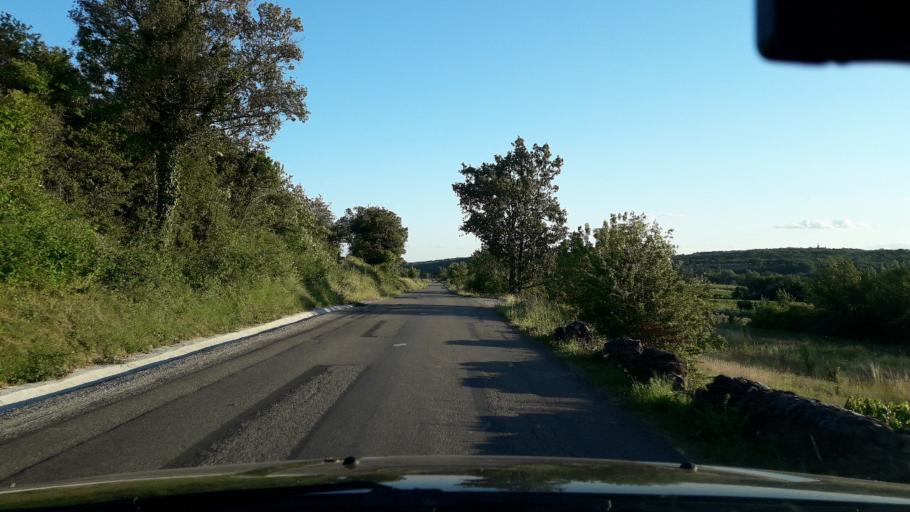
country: FR
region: Rhone-Alpes
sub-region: Departement de l'Ardeche
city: Lavilledieu
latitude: 44.6023
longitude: 4.4663
